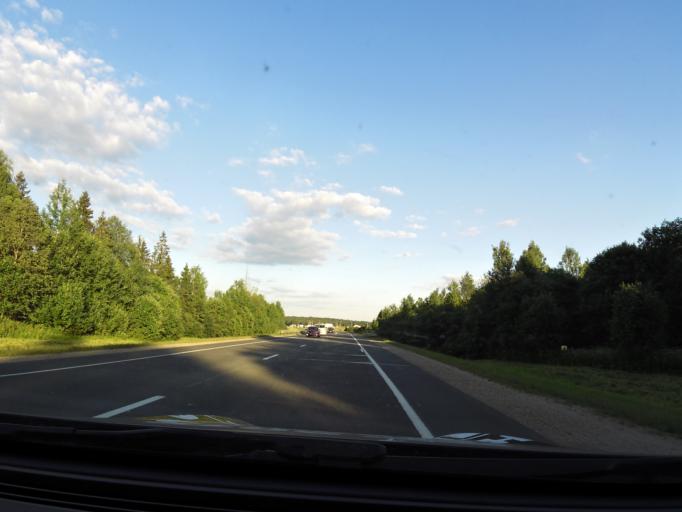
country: RU
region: Vologda
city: Vologda
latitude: 59.0770
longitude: 40.0188
